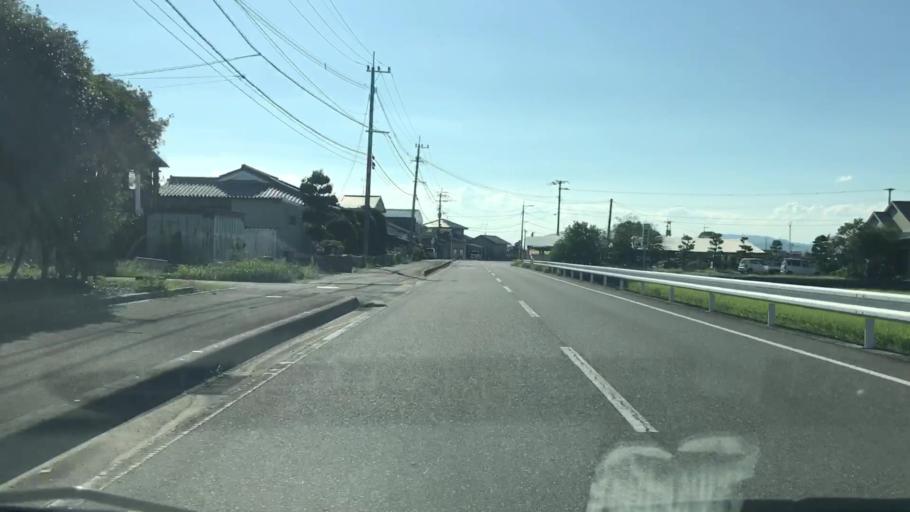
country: JP
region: Saga Prefecture
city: Saga-shi
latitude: 33.1909
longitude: 130.2836
